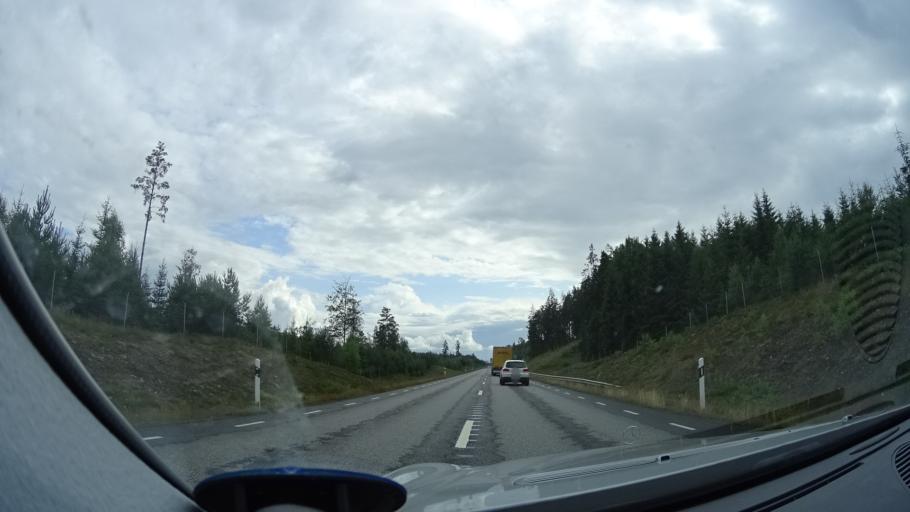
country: SE
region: Blekinge
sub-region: Karlshamns Kommun
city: Svangsta
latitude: 56.2921
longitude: 14.8770
